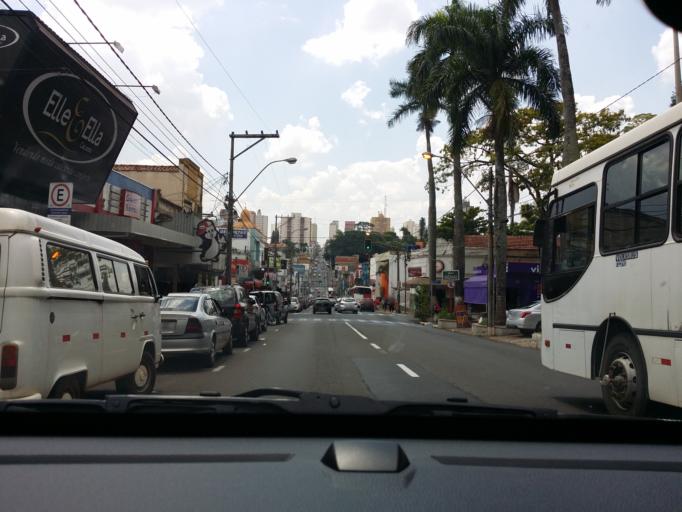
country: BR
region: Sao Paulo
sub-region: Sao Carlos
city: Sao Carlos
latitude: -22.0230
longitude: -47.8906
